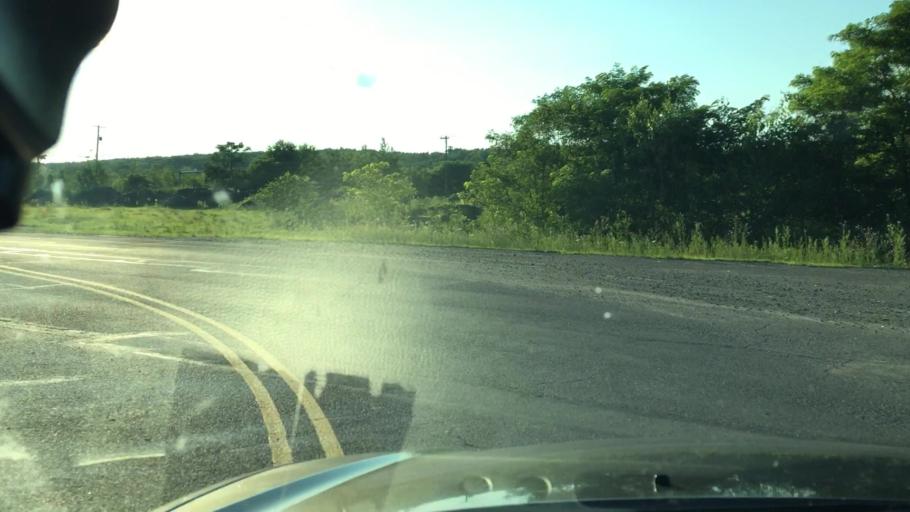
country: US
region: Pennsylvania
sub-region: Luzerne County
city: Harleigh
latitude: 40.9924
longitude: -75.9816
